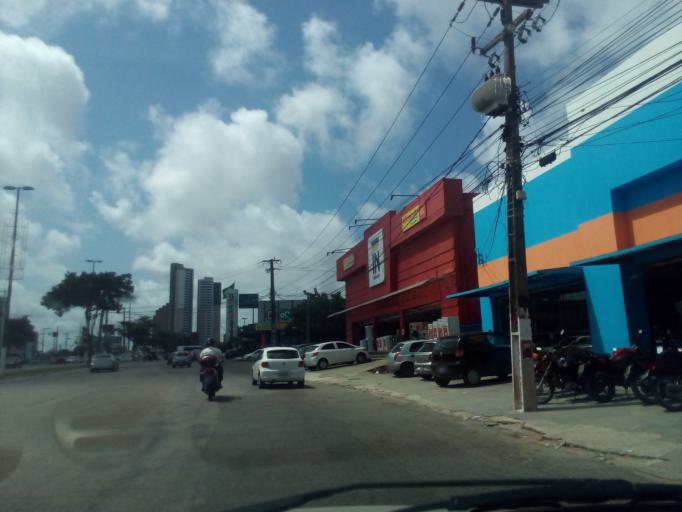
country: BR
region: Rio Grande do Norte
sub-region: Natal
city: Natal
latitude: -5.8507
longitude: -35.2051
